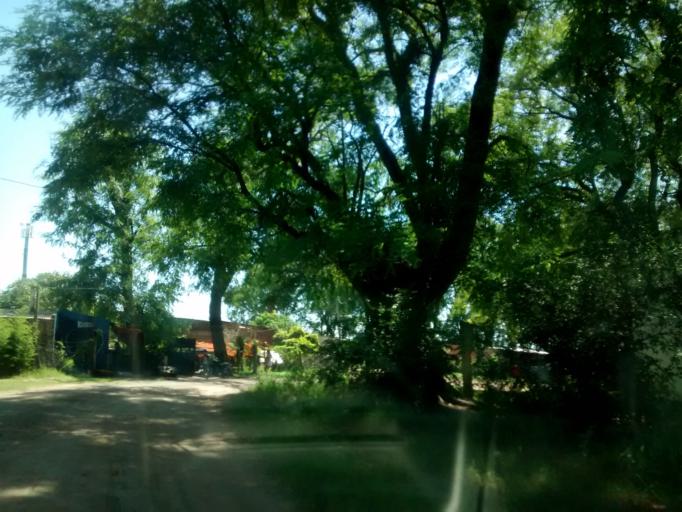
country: AR
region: Chaco
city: Fontana
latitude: -27.4100
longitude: -59.0003
